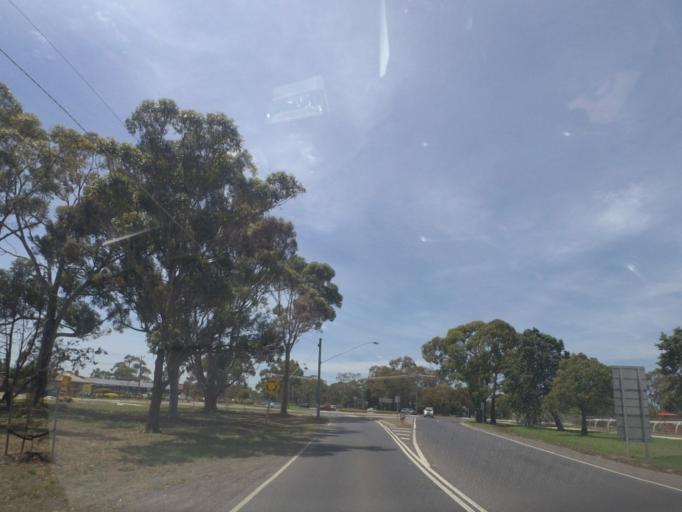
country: AU
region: Victoria
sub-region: Wyndham
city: Werribee
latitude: -37.9024
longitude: 144.6501
